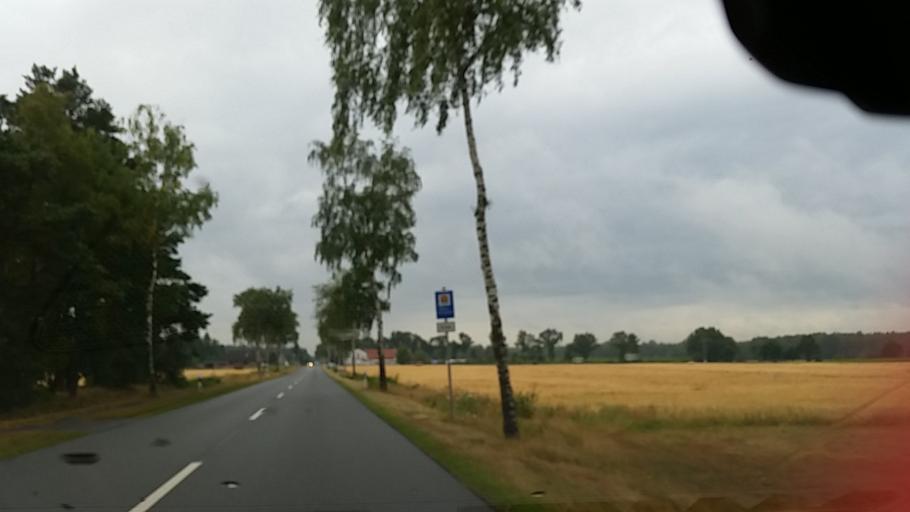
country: DE
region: Lower Saxony
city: Schoneworde
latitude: 52.6274
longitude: 10.6897
